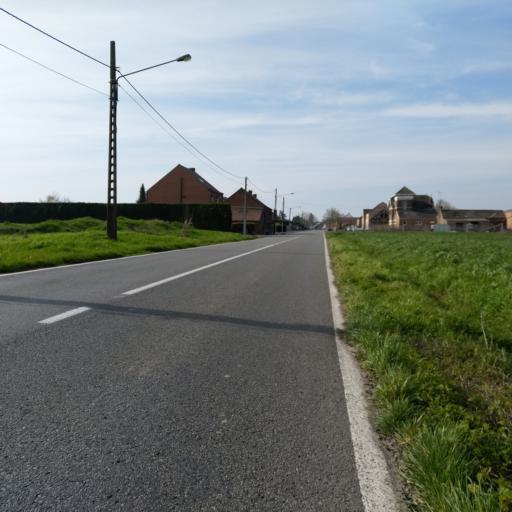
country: BE
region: Wallonia
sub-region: Province du Hainaut
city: Frameries
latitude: 50.3634
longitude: 3.8930
